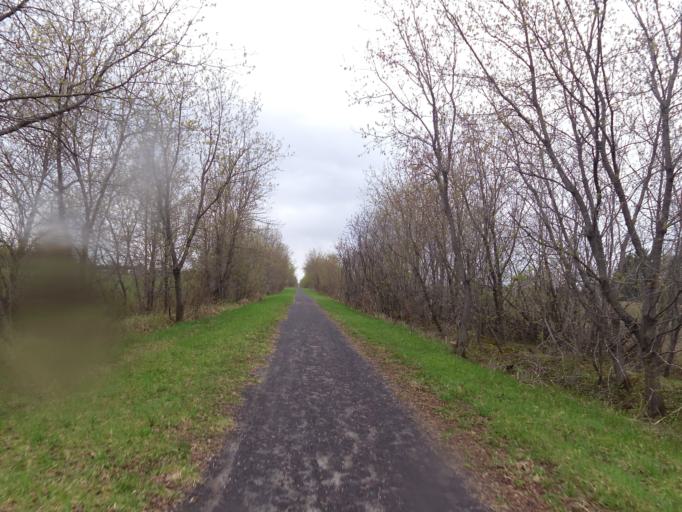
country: CA
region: Ontario
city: Bourget
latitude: 45.4393
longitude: -75.1847
